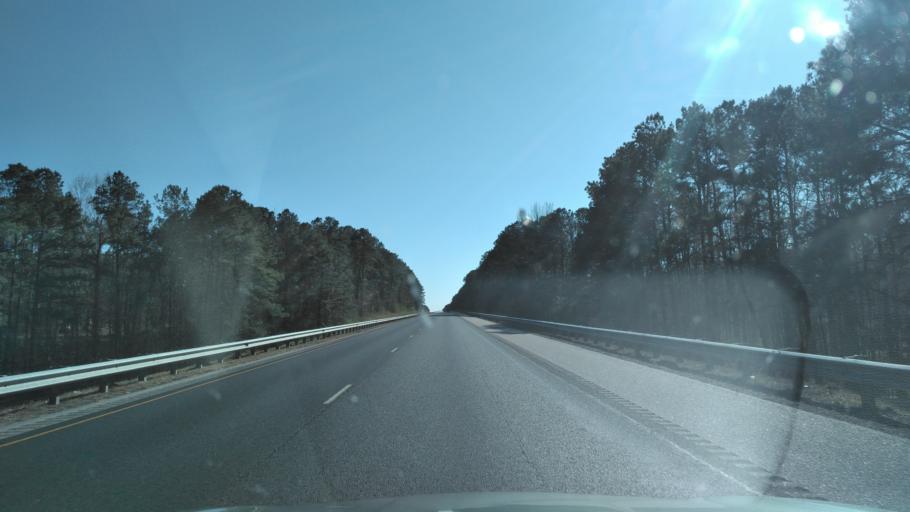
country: US
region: Alabama
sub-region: Butler County
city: Georgiana
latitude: 31.6974
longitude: -86.7437
